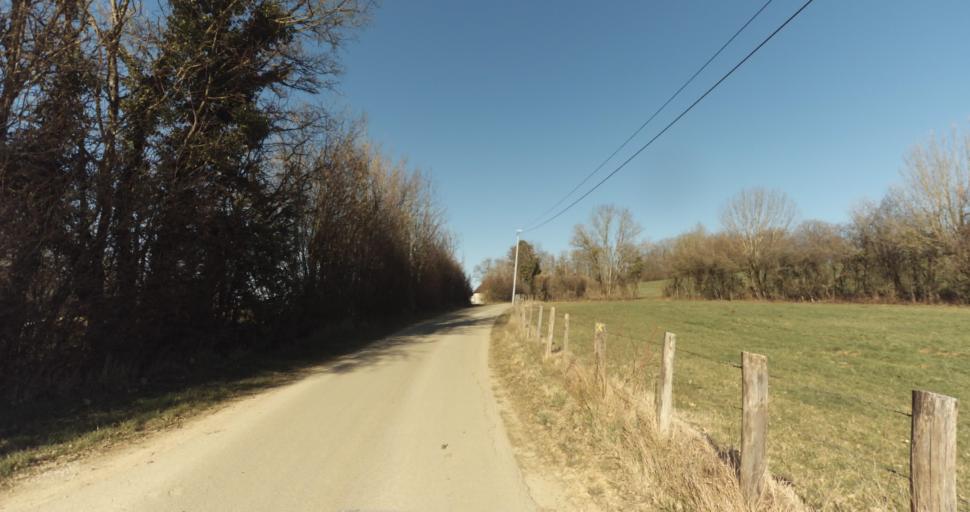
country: FR
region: Franche-Comte
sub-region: Departement du Jura
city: Montmorot
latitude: 46.6987
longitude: 5.5178
